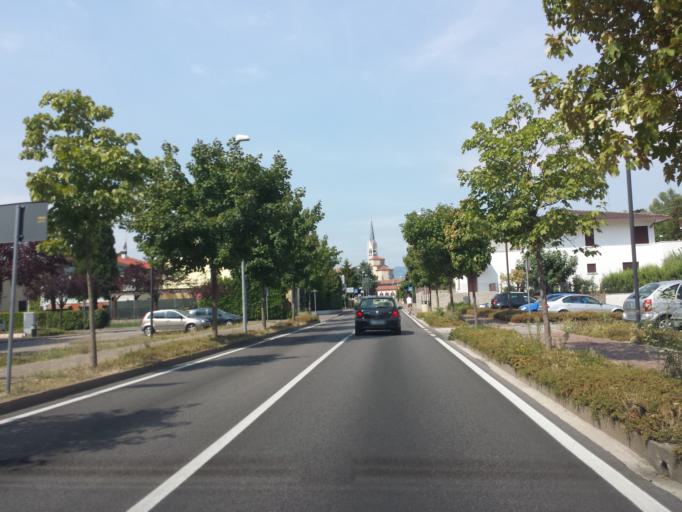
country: IT
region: Veneto
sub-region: Provincia di Vicenza
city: Montecchio Maggiore-Alte Ceccato
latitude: 45.5054
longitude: 11.4153
